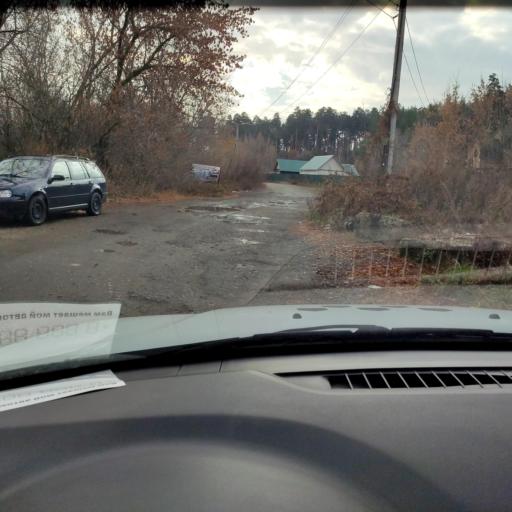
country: RU
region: Samara
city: Tol'yatti
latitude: 53.5270
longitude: 49.3916
